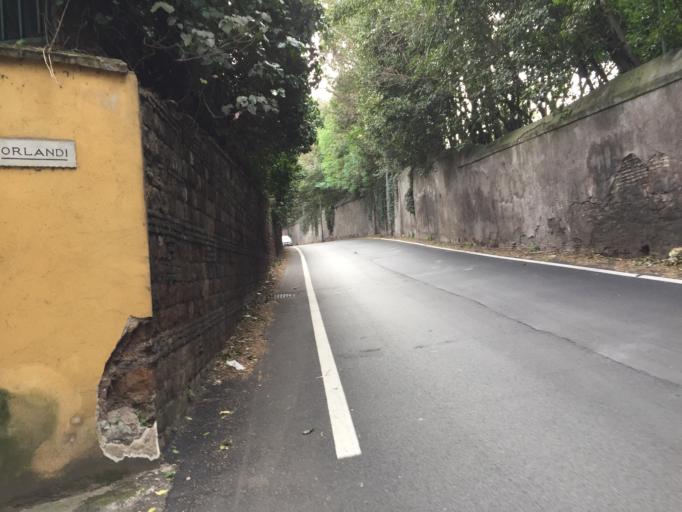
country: VA
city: Vatican City
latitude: 41.8897
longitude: 12.4583
